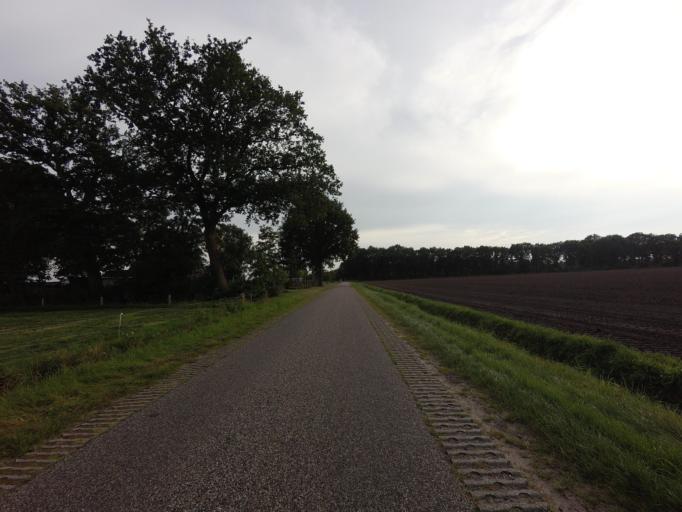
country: DE
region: Lower Saxony
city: Wielen
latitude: 52.5840
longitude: 6.6774
